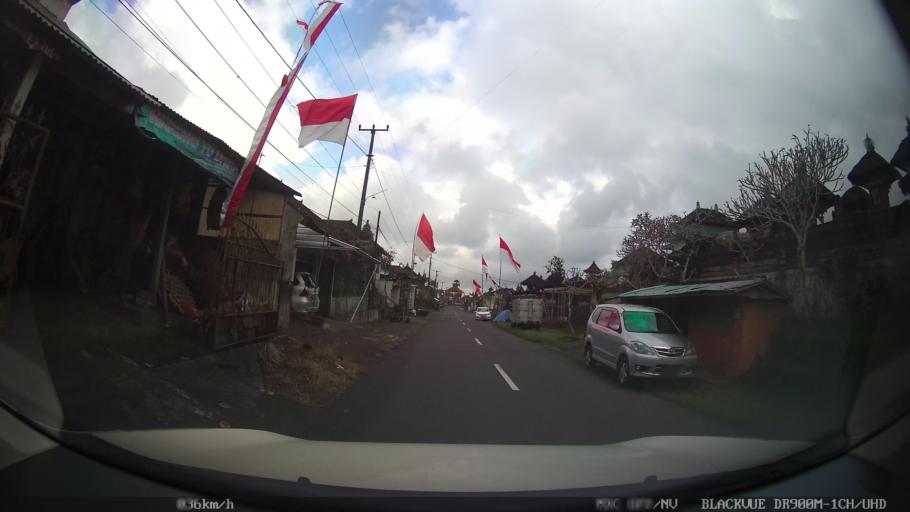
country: ID
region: Bali
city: Peneng
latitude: -8.3677
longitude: 115.1783
